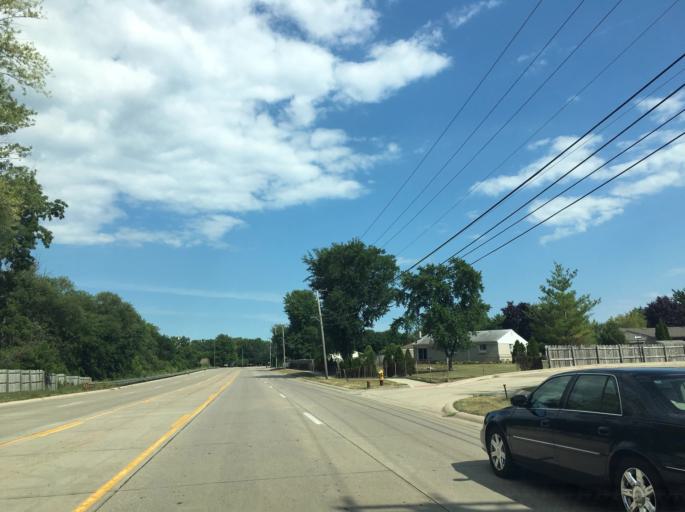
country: US
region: Michigan
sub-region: Macomb County
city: Clinton
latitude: 42.6099
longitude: -82.9272
